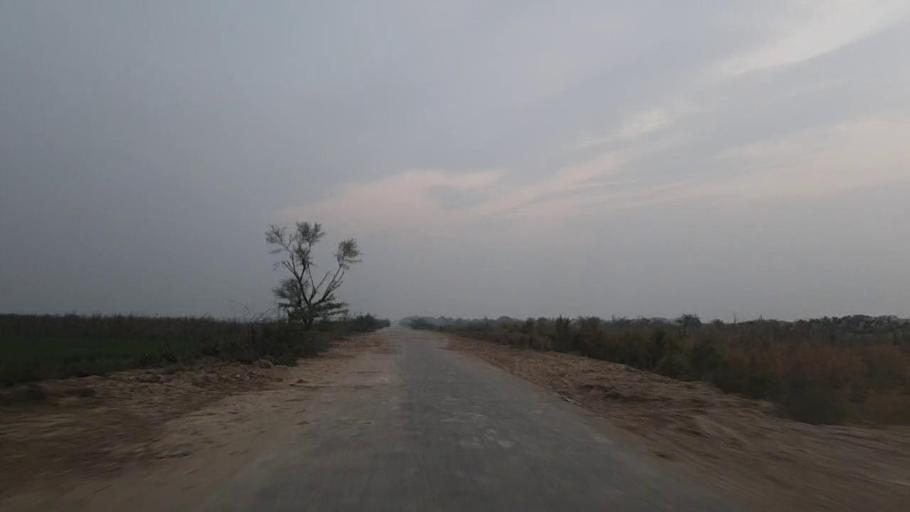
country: PK
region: Sindh
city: Jam Sahib
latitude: 26.3344
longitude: 68.5494
